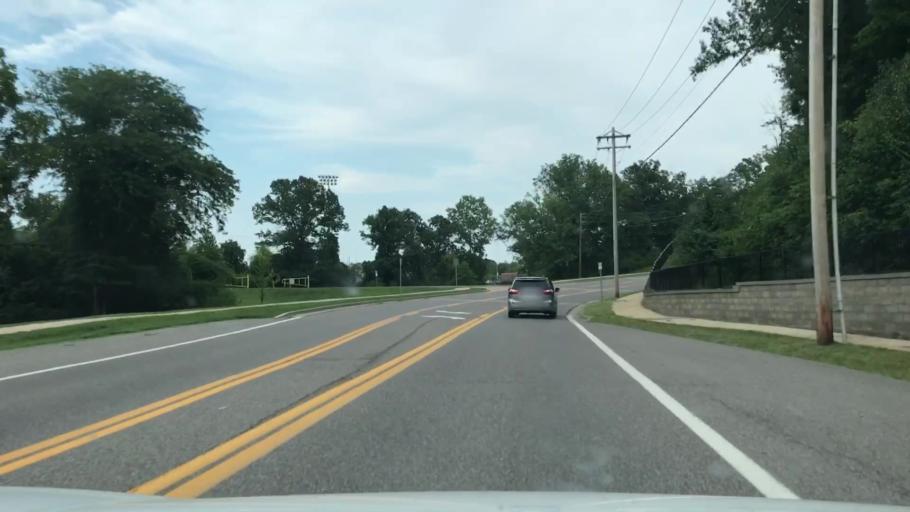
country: US
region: Missouri
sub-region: Saint Louis County
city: Clarkson Valley
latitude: 38.6237
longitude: -90.5872
